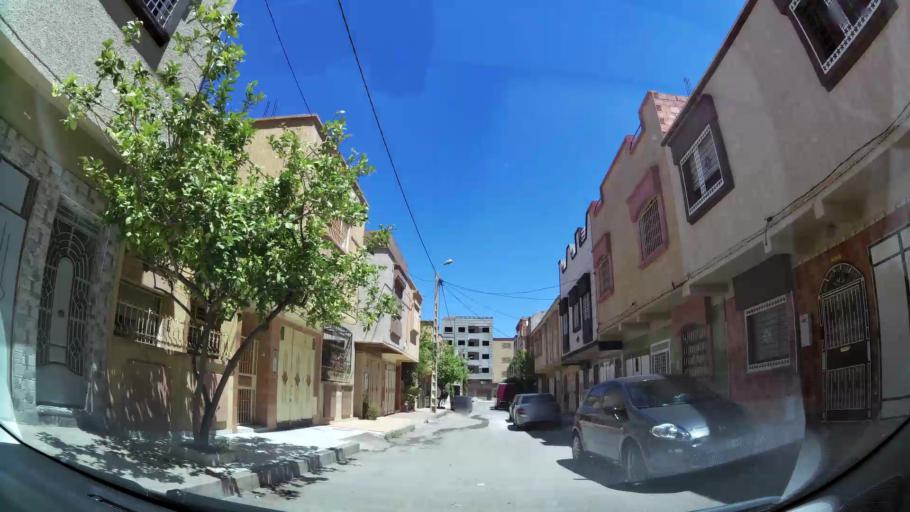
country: MA
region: Oriental
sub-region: Oujda-Angad
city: Oujda
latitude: 34.6697
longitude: -1.8835
